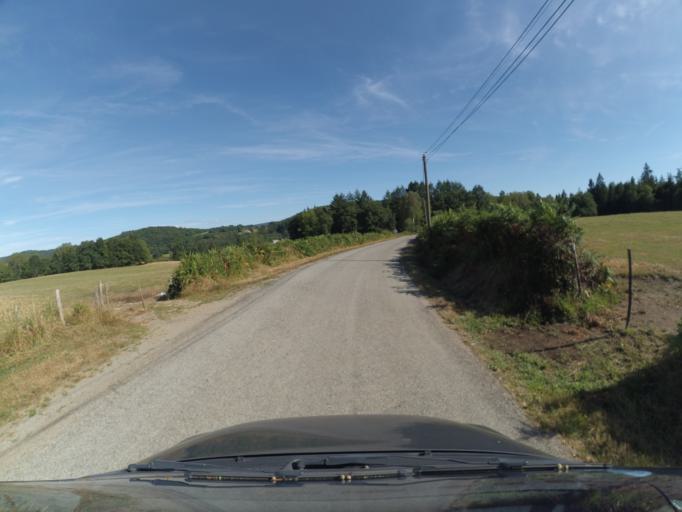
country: FR
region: Limousin
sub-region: Departement de la Haute-Vienne
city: Eymoutiers
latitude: 45.7090
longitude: 1.8627
